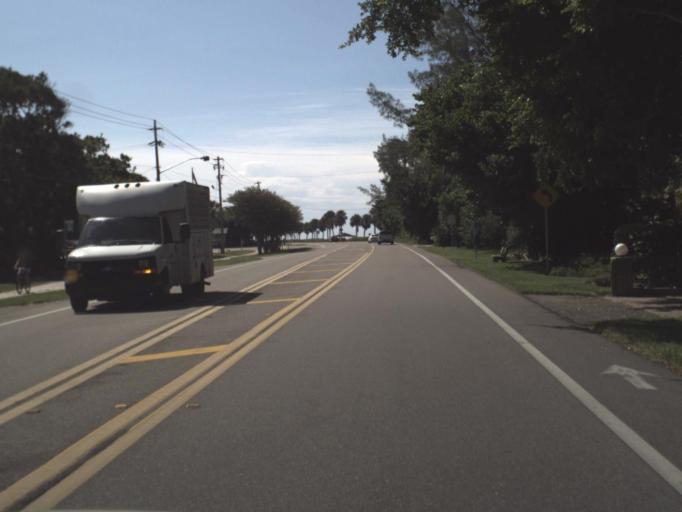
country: US
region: Florida
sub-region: Manatee County
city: Longboat Key
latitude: 27.3886
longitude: -82.6408
